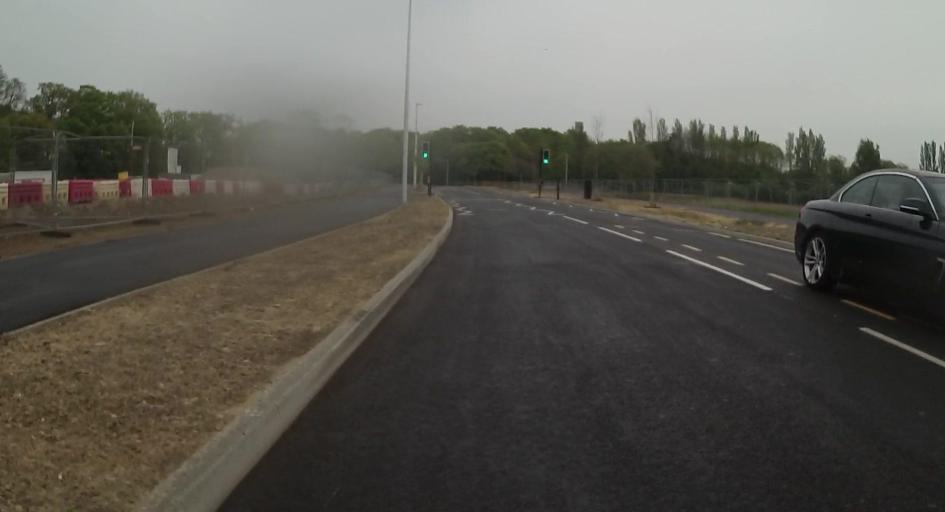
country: GB
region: England
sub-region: Hampshire
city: Eversley
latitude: 51.3747
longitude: -0.8872
